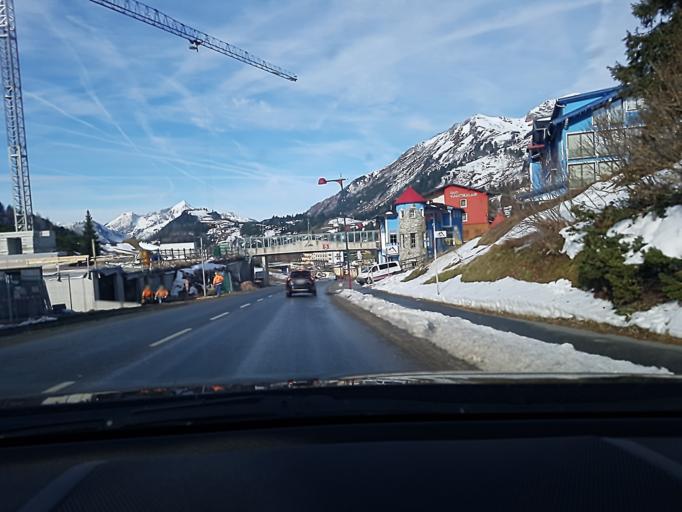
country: AT
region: Salzburg
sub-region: Politischer Bezirk Sankt Johann im Pongau
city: Untertauern
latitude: 47.2491
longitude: 13.5556
